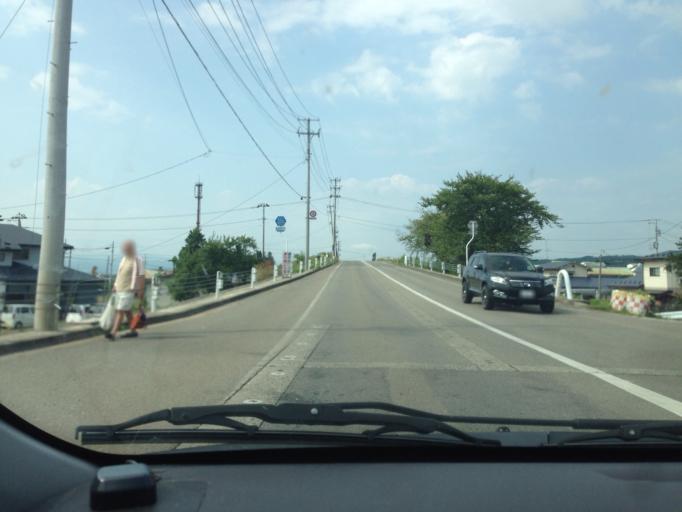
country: JP
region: Fukushima
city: Kitakata
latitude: 37.6457
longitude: 139.8621
